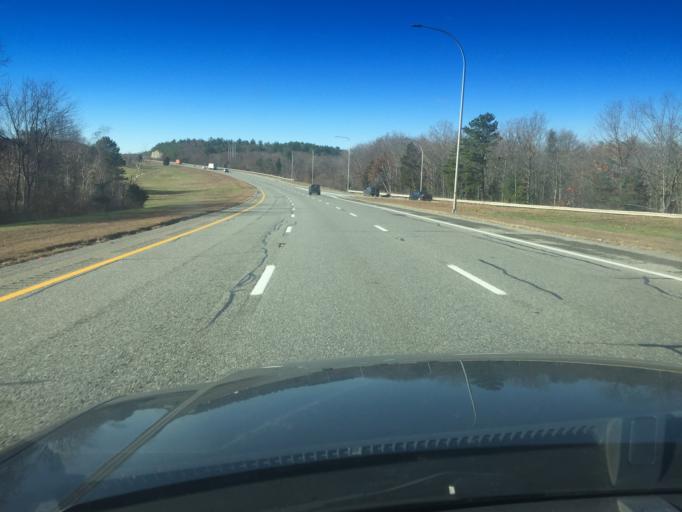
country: US
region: Rhode Island
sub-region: Providence County
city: Cumberland Hill
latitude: 41.9433
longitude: -71.4804
